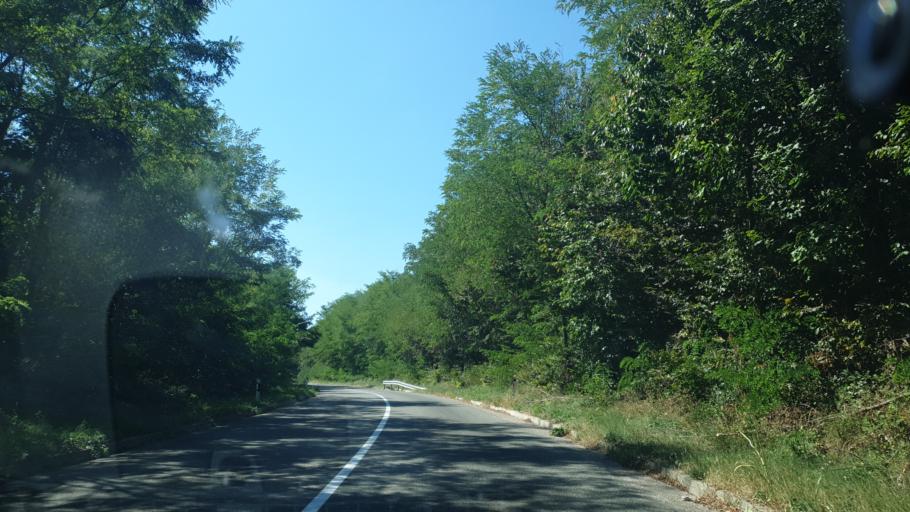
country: RS
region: Central Serbia
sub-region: Kolubarski Okrug
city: Mionica
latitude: 44.1747
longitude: 20.0056
